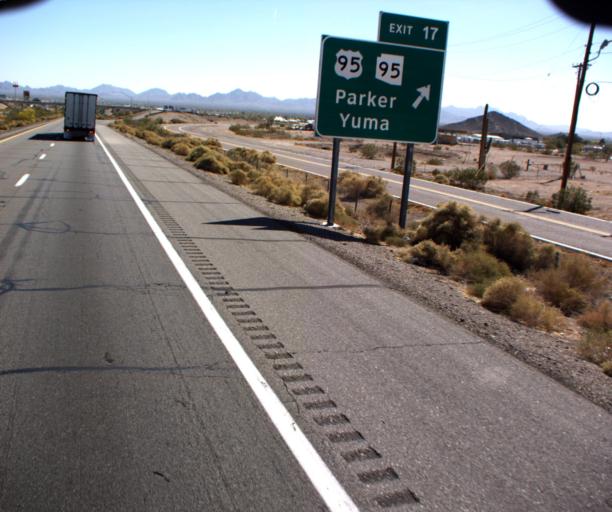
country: US
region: Arizona
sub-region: La Paz County
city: Quartzsite
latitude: 33.6588
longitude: -114.2461
